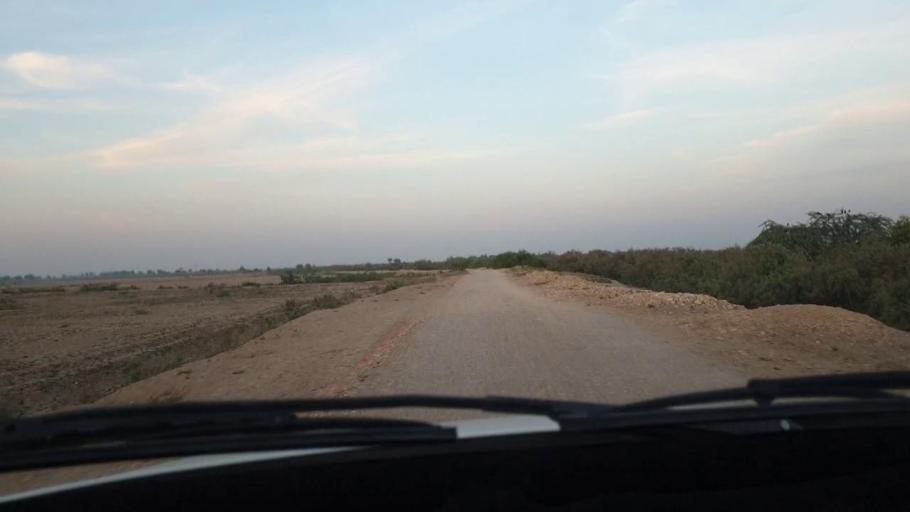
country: PK
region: Sindh
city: Tando Muhammad Khan
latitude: 25.0921
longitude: 68.3867
